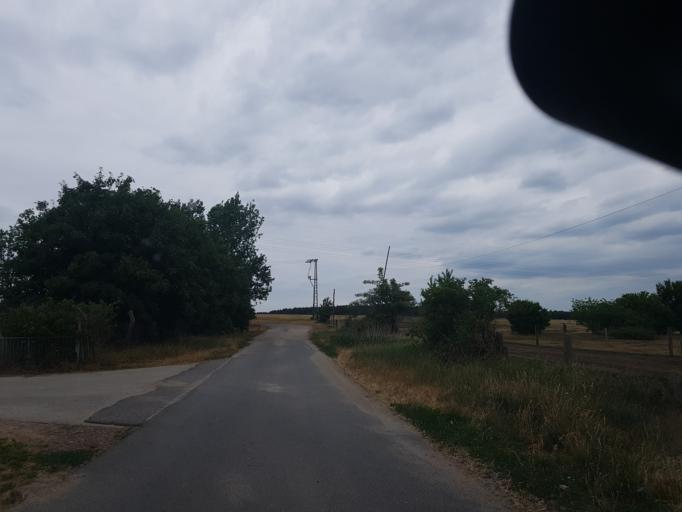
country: DE
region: Brandenburg
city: Treuenbrietzen
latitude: 52.0786
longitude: 12.8091
